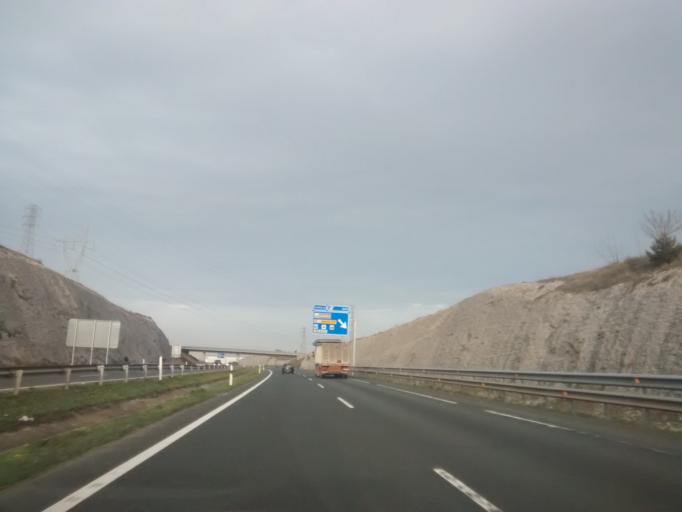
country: ES
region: Basque Country
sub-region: Provincia de Alava
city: Gasteiz / Vitoria
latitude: 42.8315
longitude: -2.7561
